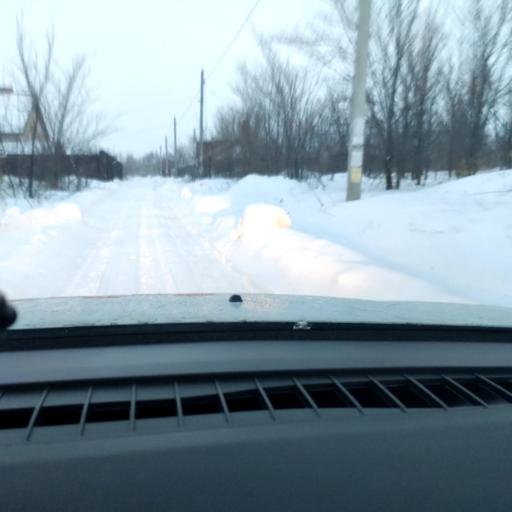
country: RU
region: Samara
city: Dubovyy Umet
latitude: 53.0291
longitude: 50.2301
